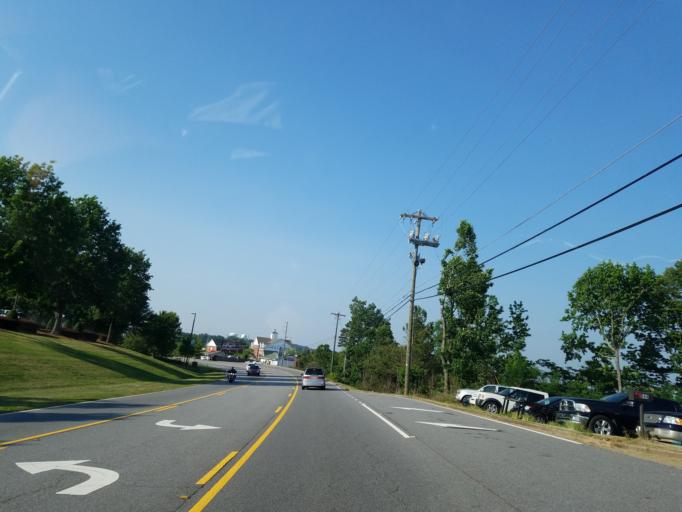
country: US
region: Georgia
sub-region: Forsyth County
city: Cumming
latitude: 34.1916
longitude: -84.1361
